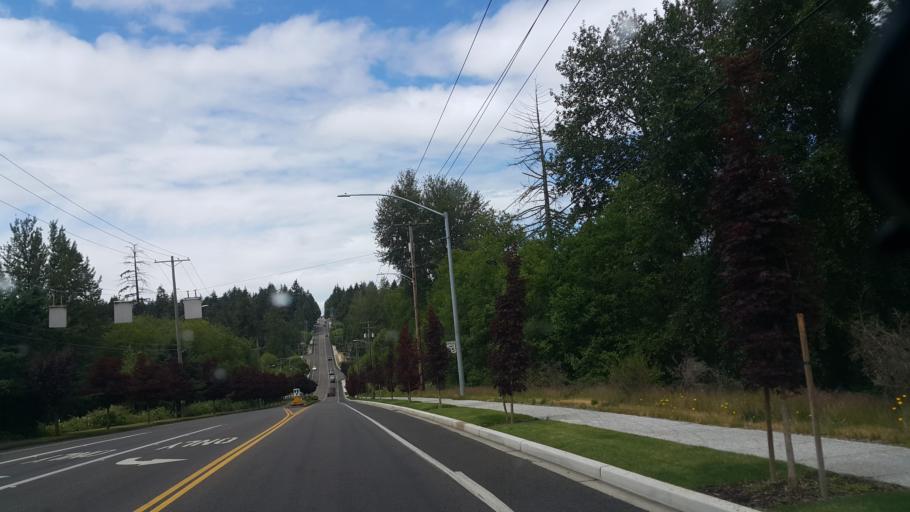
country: US
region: Washington
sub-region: Pierce County
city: Fircrest
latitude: 47.2212
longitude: -122.5059
